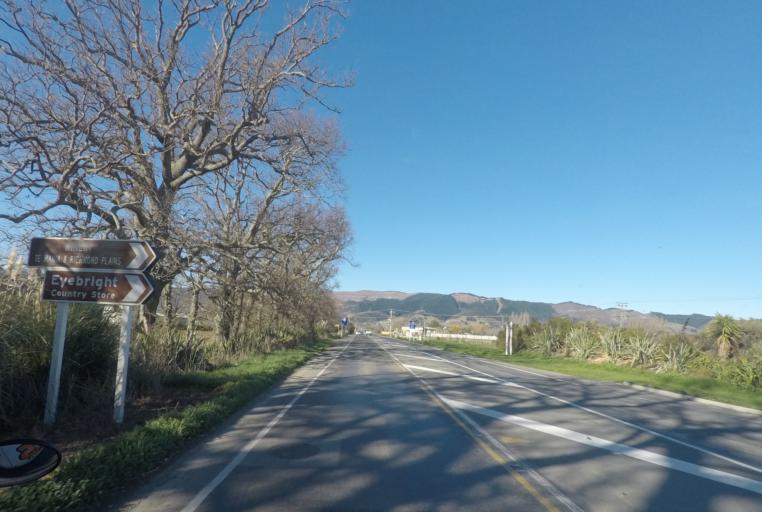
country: NZ
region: Tasman
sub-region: Tasman District
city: Richmond
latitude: -41.3269
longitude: 173.1710
